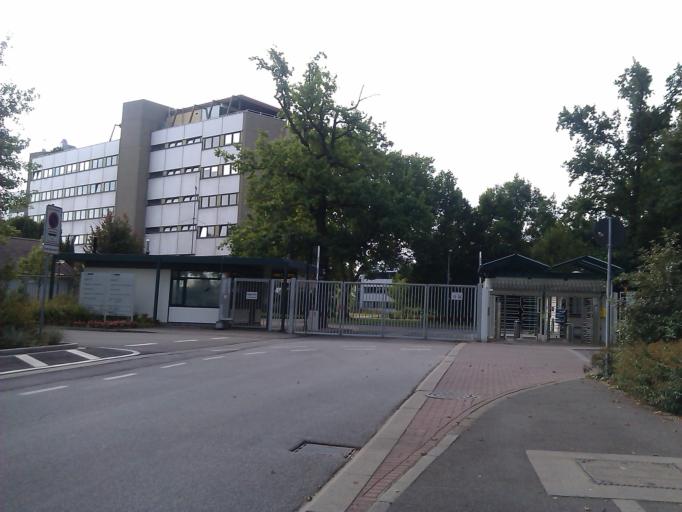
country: DE
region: Rheinland-Pfalz
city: Limburgerhof
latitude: 49.4123
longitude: 8.3944
